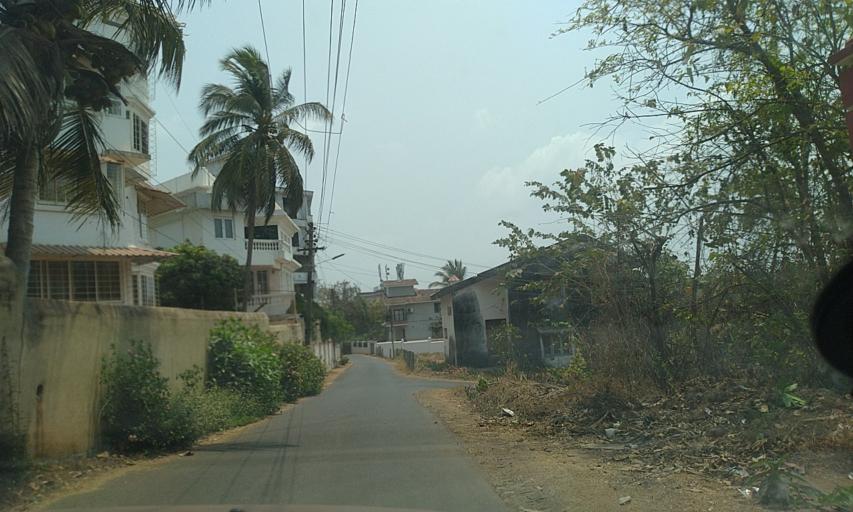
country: IN
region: Goa
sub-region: North Goa
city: Panaji
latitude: 15.5213
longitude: 73.8210
